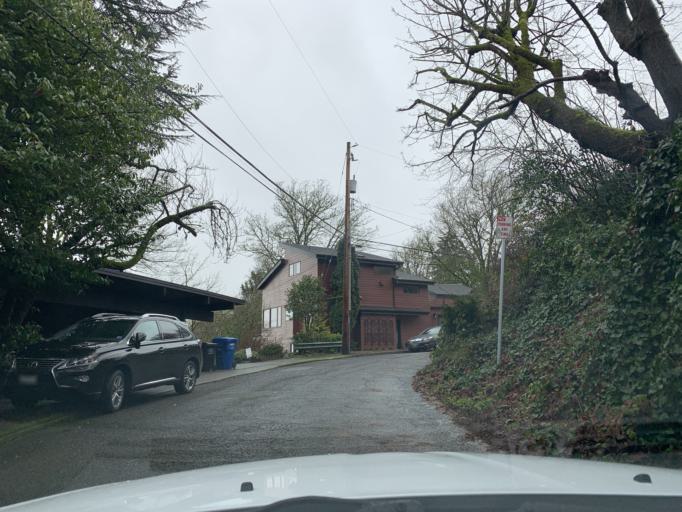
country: US
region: Washington
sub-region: King County
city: Seattle
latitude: 47.6055
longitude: -122.2888
